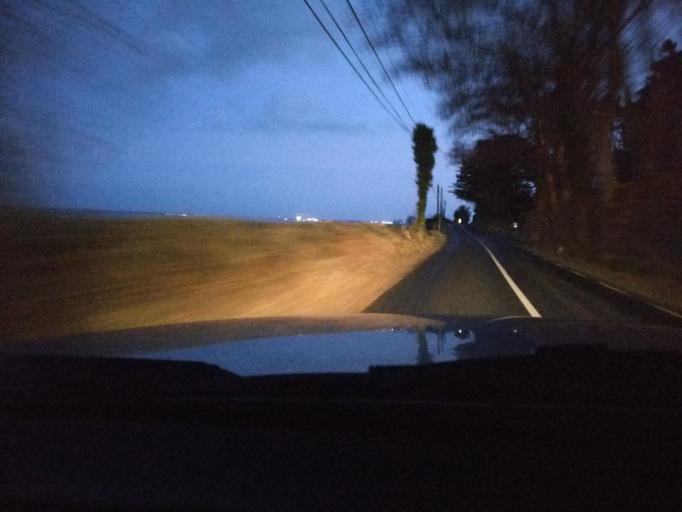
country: IE
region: Leinster
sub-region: Lu
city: Carlingford
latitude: 54.0571
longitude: -6.1996
